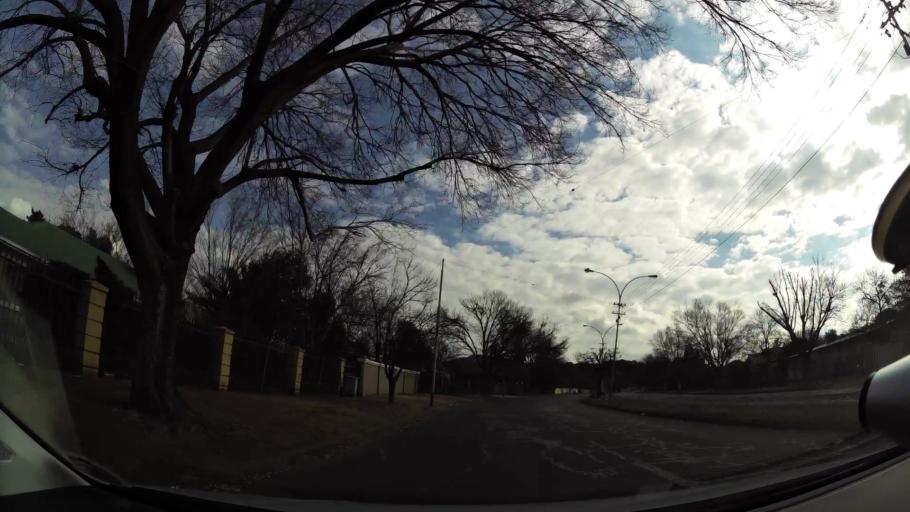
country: ZA
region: Orange Free State
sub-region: Mangaung Metropolitan Municipality
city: Bloemfontein
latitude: -29.0805
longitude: 26.2384
